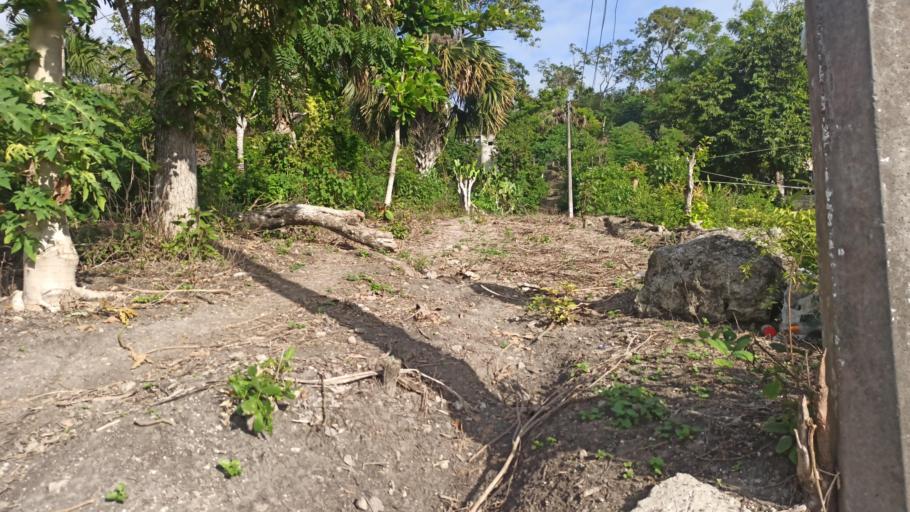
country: MX
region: Veracruz
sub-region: Papantla
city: Residencial Tajin
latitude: 20.6451
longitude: -97.3599
